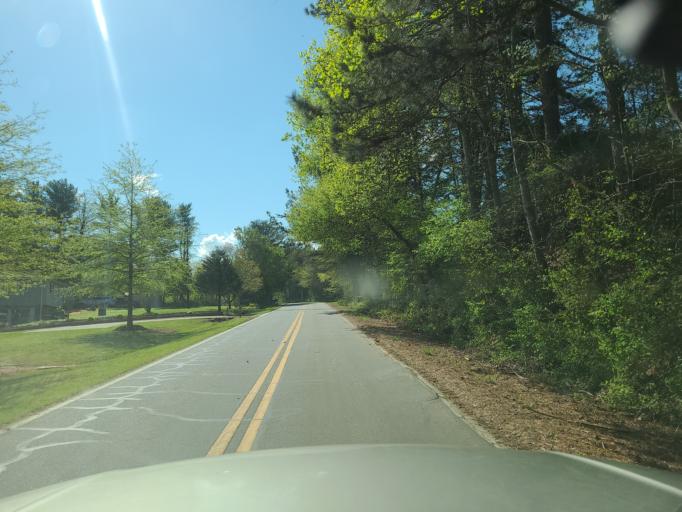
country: US
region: North Carolina
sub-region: Rutherford County
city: Spindale
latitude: 35.2976
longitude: -81.9633
